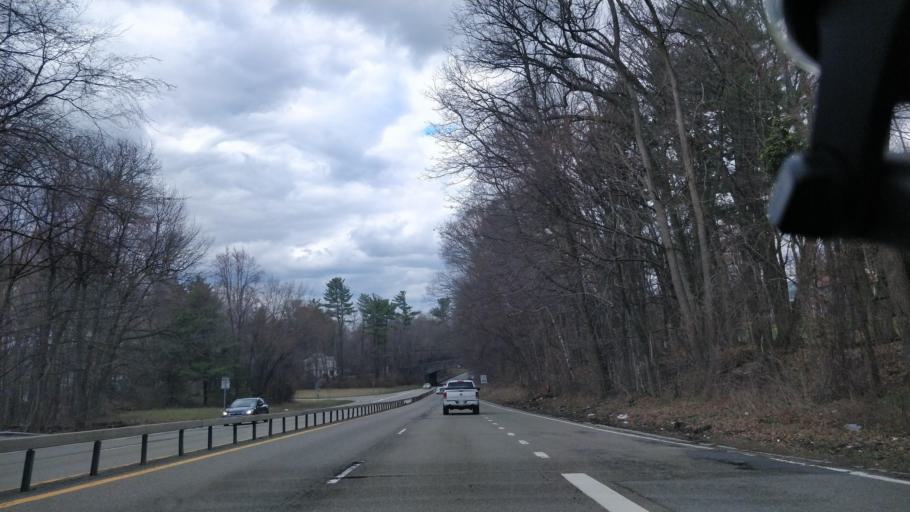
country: US
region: New York
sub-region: Westchester County
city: Ossining
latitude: 41.1698
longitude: -73.8390
